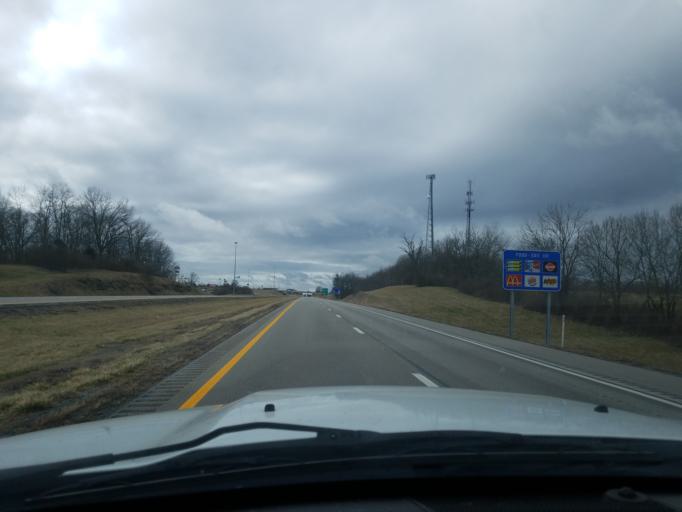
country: US
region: Kentucky
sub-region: Montgomery County
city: Mount Sterling
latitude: 38.0811
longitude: -83.9392
